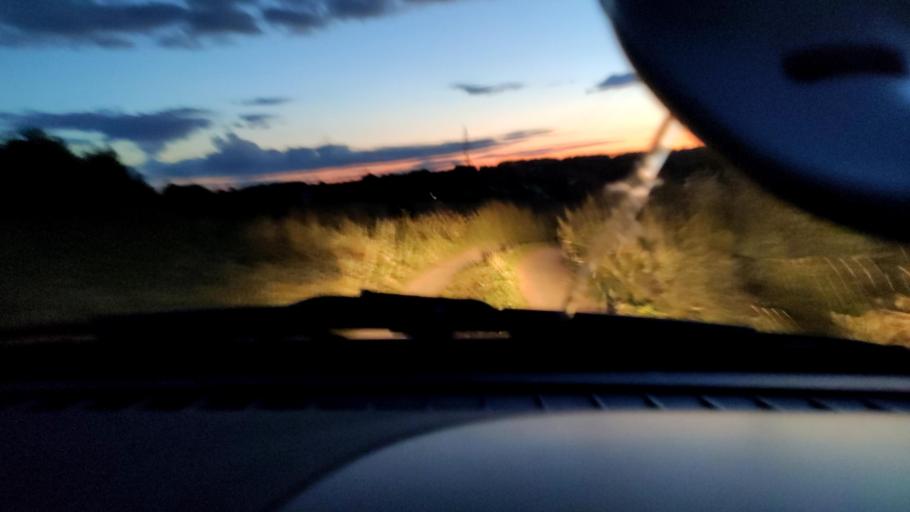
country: RU
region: Perm
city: Froly
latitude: 57.9462
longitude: 56.2524
